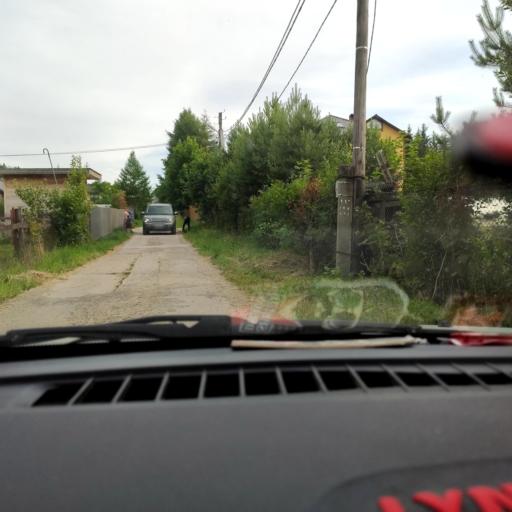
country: RU
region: Perm
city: Polazna
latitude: 58.2507
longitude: 56.2534
